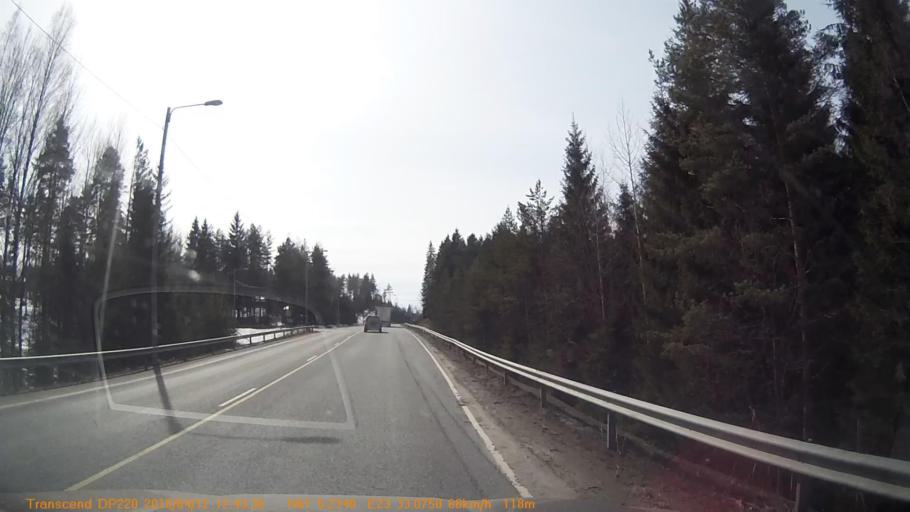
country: FI
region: Pirkanmaa
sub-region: Etelae-Pirkanmaa
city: Urjala
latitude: 61.0870
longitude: 23.5510
